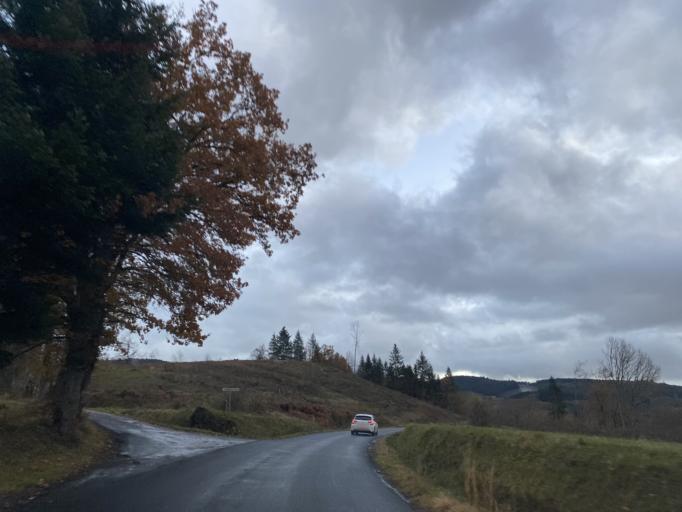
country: FR
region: Auvergne
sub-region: Departement du Puy-de-Dome
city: Cunlhat
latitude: 45.6192
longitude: 3.5654
